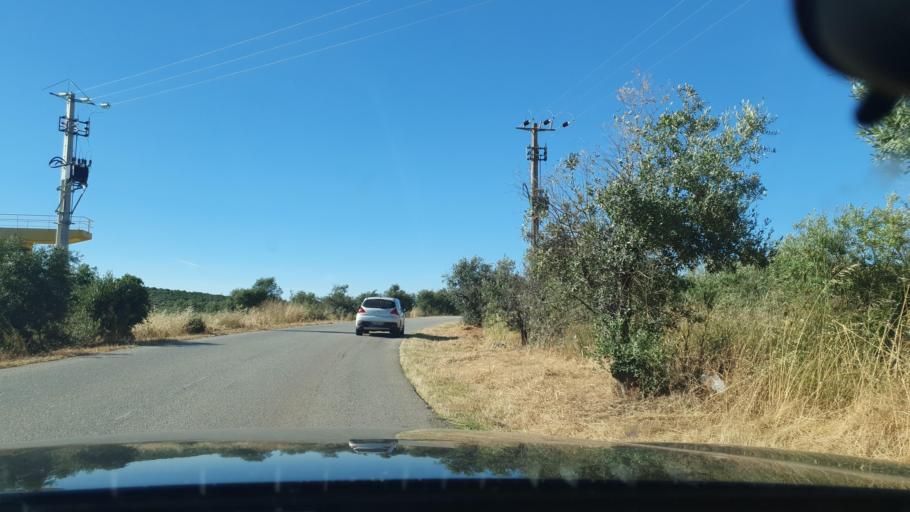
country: PT
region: Evora
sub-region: Vila Vicosa
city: Vila Vicosa
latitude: 38.7481
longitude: -7.4090
